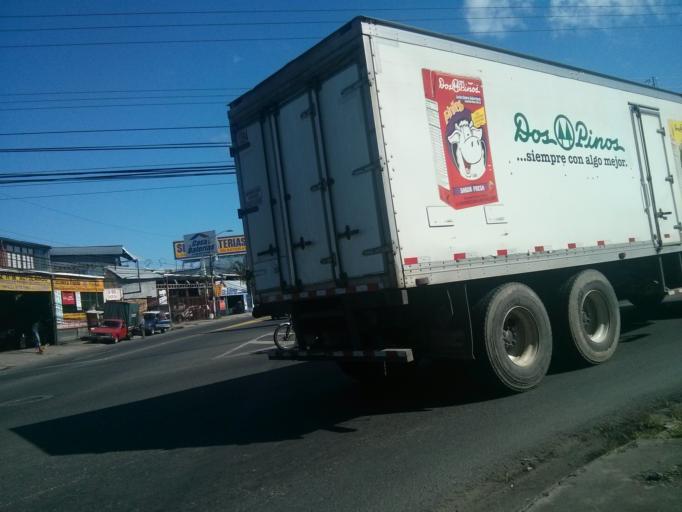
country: CR
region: San Jose
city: San Rafael Arriba
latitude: 9.9006
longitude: -84.0615
